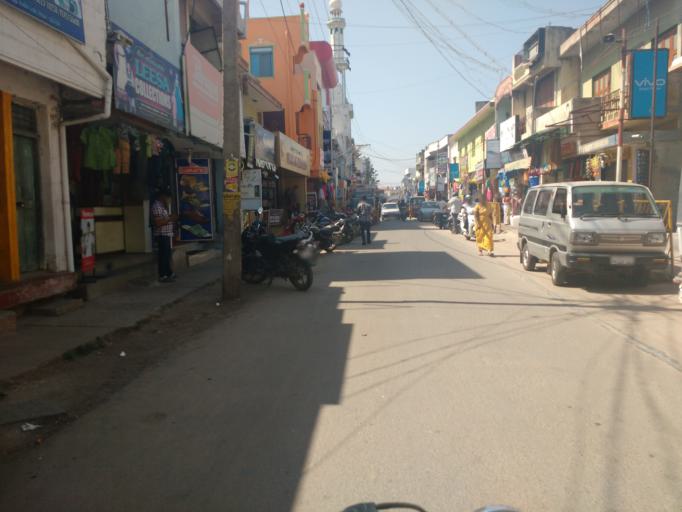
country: IN
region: Tamil Nadu
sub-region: Krishnagiri
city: Hosur
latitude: 12.7328
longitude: 77.8283
